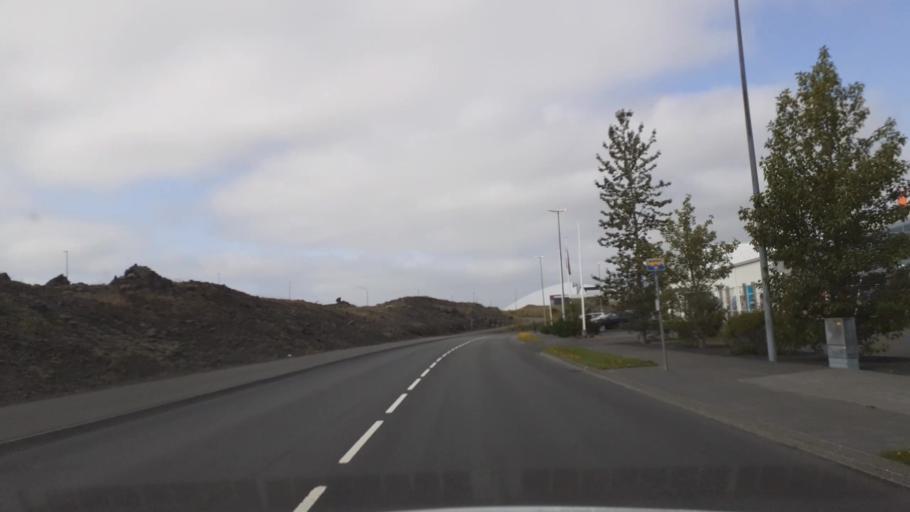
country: IS
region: Capital Region
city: Gardabaer
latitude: 64.0762
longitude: -21.9226
